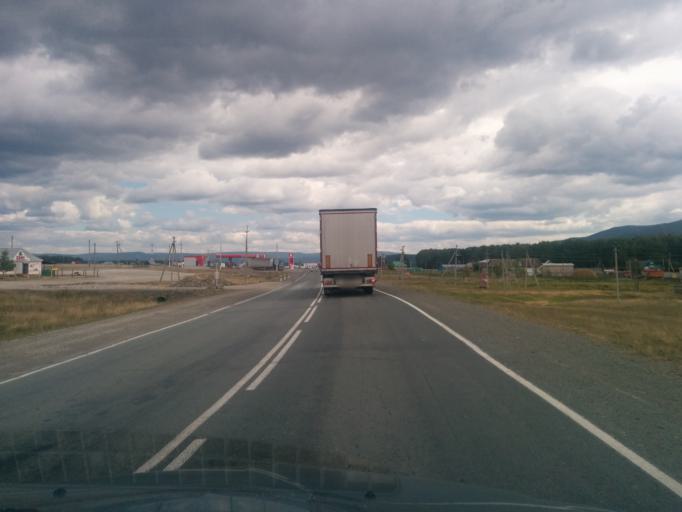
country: RU
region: Bashkortostan
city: Lomovka
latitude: 53.8829
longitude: 58.1015
